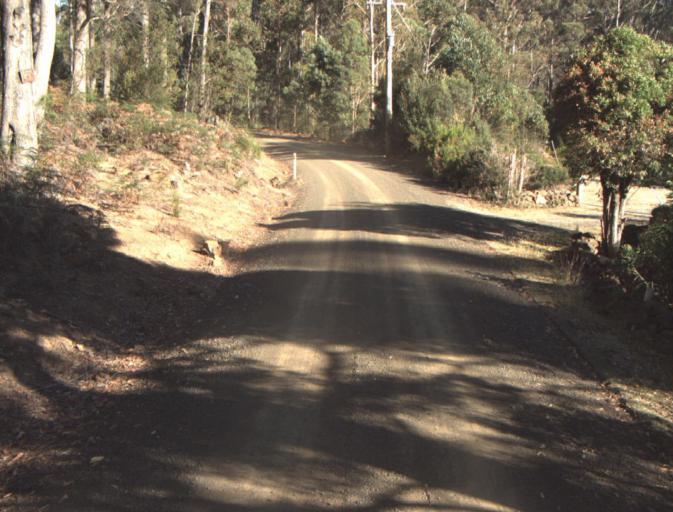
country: AU
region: Tasmania
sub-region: Launceston
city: Mayfield
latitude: -41.2922
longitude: 147.1831
